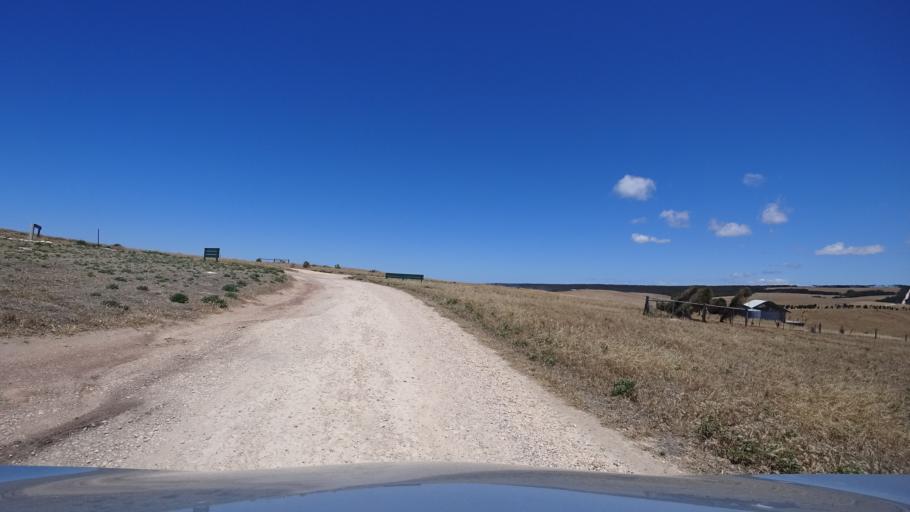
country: AU
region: South Australia
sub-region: Yankalilla
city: Normanville
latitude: -35.8423
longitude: 138.1315
